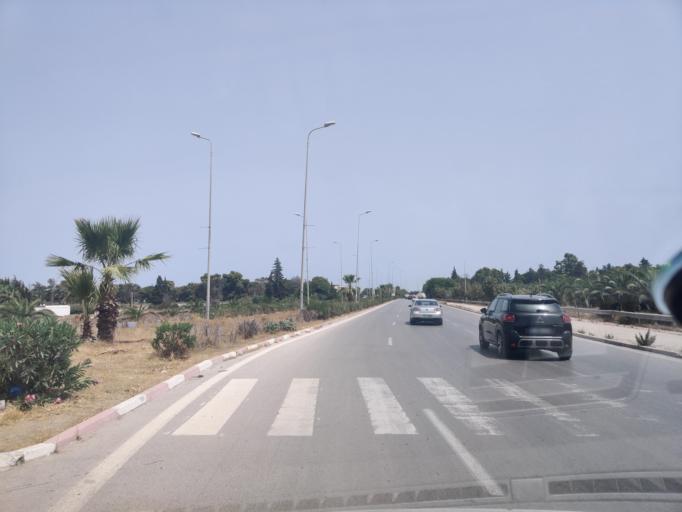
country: TN
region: Tunis
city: Carthage
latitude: 36.8567
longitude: 10.3112
